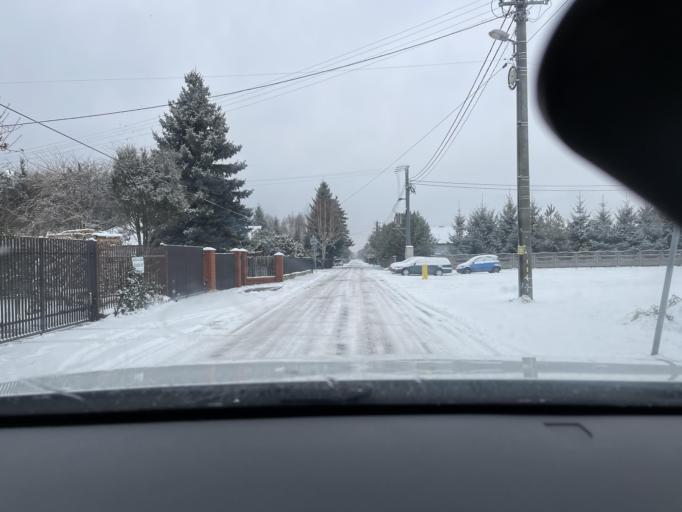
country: PL
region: Masovian Voivodeship
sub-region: Powiat zyrardowski
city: Zyrardow
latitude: 52.0303
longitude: 20.4593
